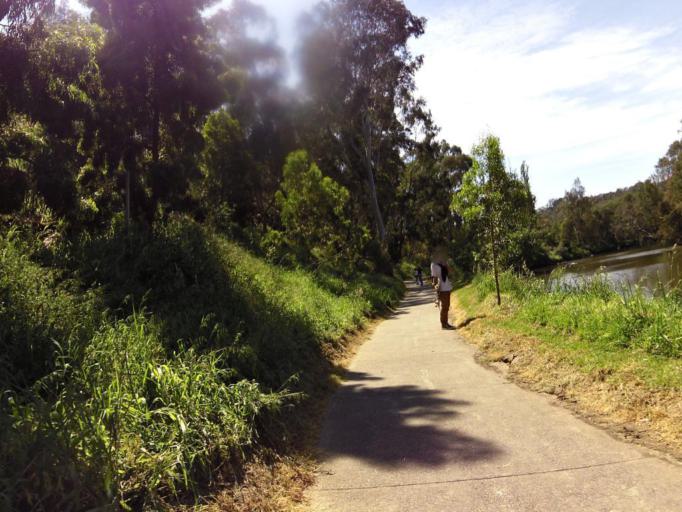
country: AU
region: Victoria
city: Abbotsford
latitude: -37.8042
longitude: 145.0000
